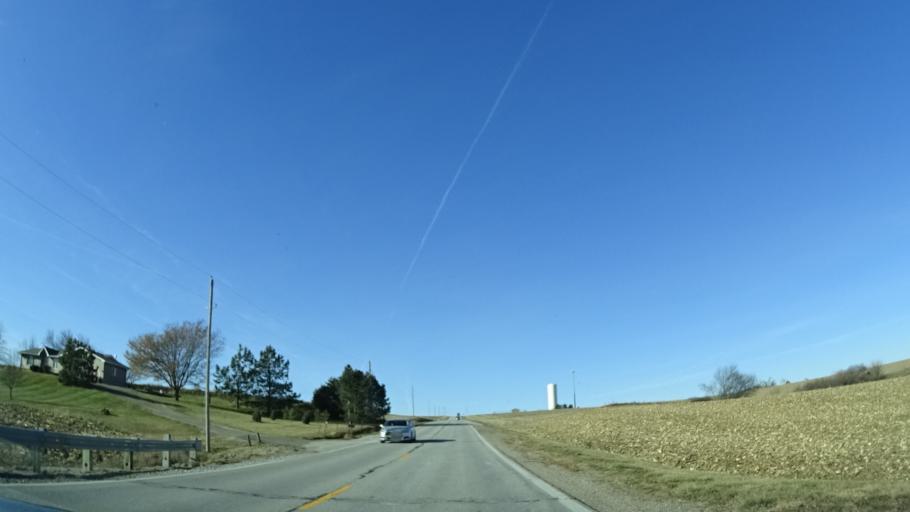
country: US
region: Nebraska
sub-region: Sarpy County
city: Springfield
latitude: 41.0890
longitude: -96.1085
